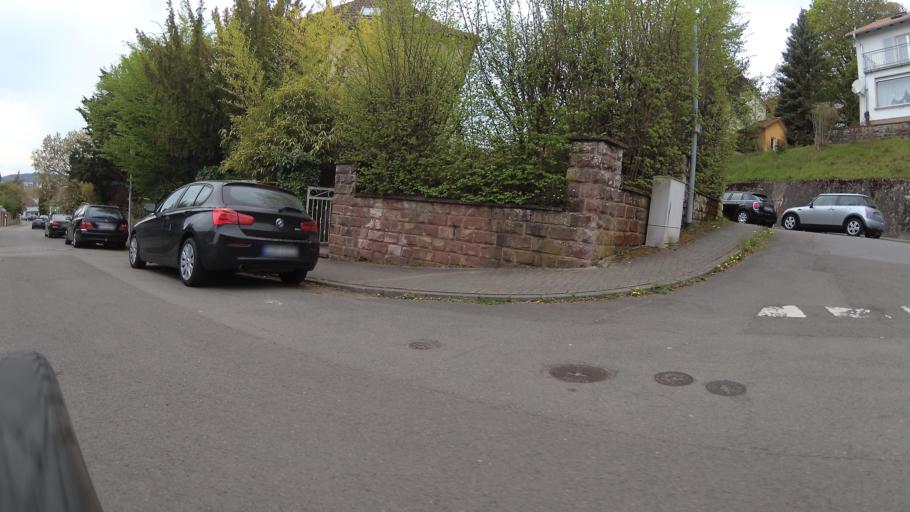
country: DE
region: Rheinland-Pfalz
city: Zweibrucken
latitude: 49.2580
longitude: 7.3718
